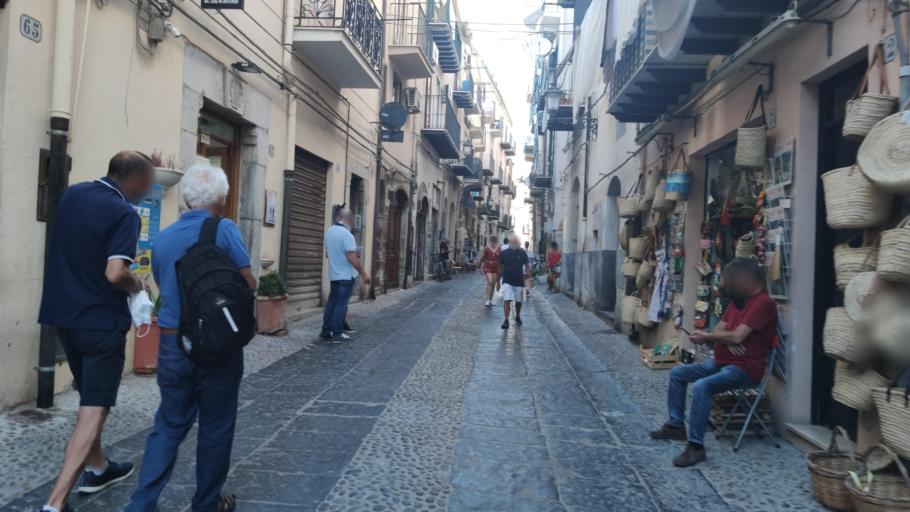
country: IT
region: Sicily
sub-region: Palermo
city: Cefalu
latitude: 38.0394
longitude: 14.0201
